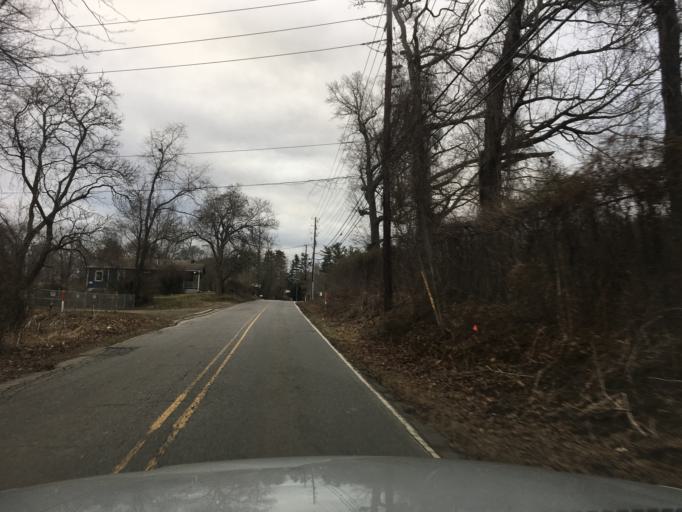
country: US
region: North Carolina
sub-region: Buncombe County
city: Asheville
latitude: 35.6002
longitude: -82.5837
